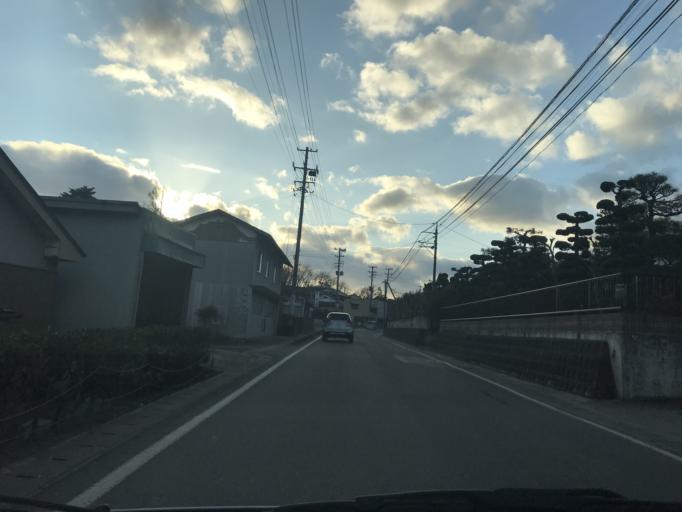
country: JP
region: Miyagi
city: Kogota
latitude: 38.6536
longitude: 141.0701
